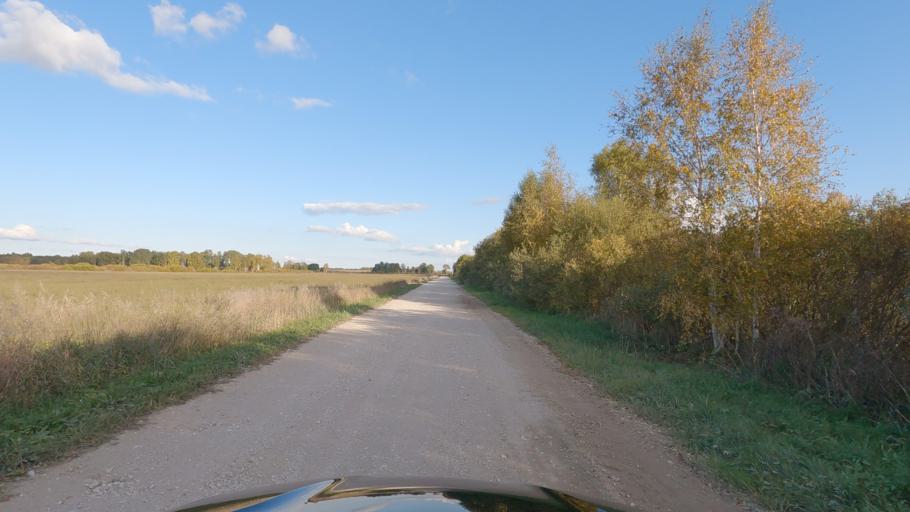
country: EE
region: Harju
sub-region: Saku vald
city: Saku
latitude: 59.2880
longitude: 24.6907
